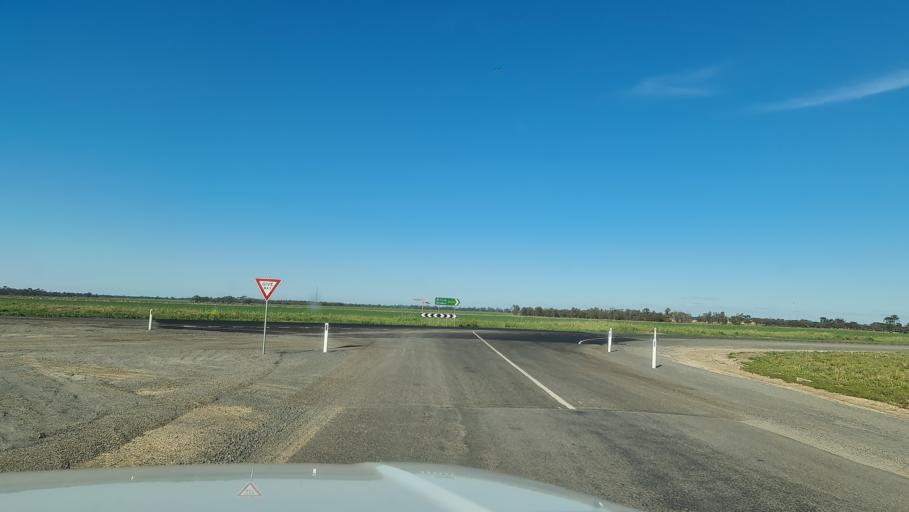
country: AU
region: Victoria
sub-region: Horsham
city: Horsham
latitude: -36.4490
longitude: 142.5699
